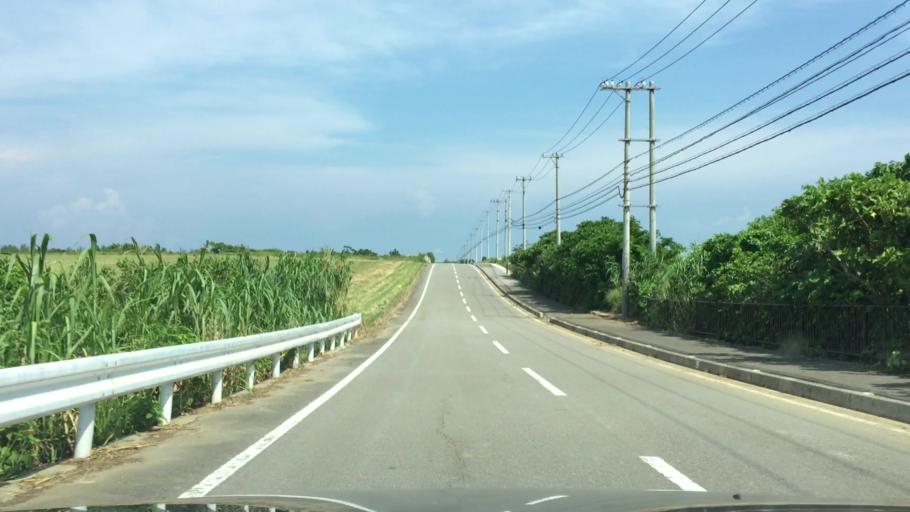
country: JP
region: Okinawa
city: Ishigaki
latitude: 24.5045
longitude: 124.2749
